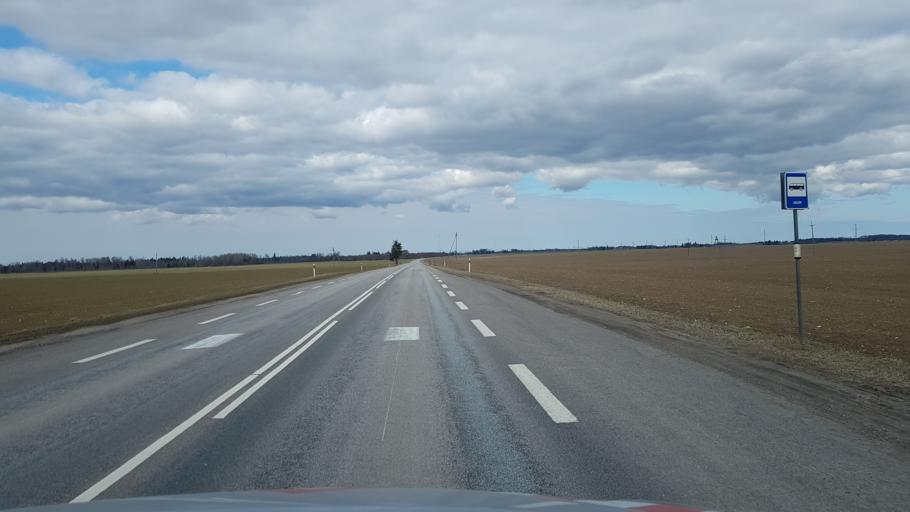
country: EE
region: Laeaene-Virumaa
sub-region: Vaeike-Maarja vald
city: Vaike-Maarja
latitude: 59.1810
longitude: 26.2667
